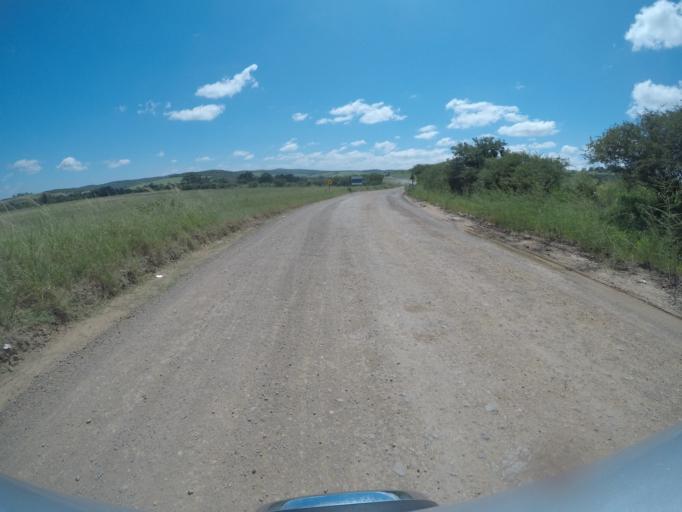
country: ZA
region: KwaZulu-Natal
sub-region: uThungulu District Municipality
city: Empangeni
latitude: -28.6618
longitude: 31.7794
